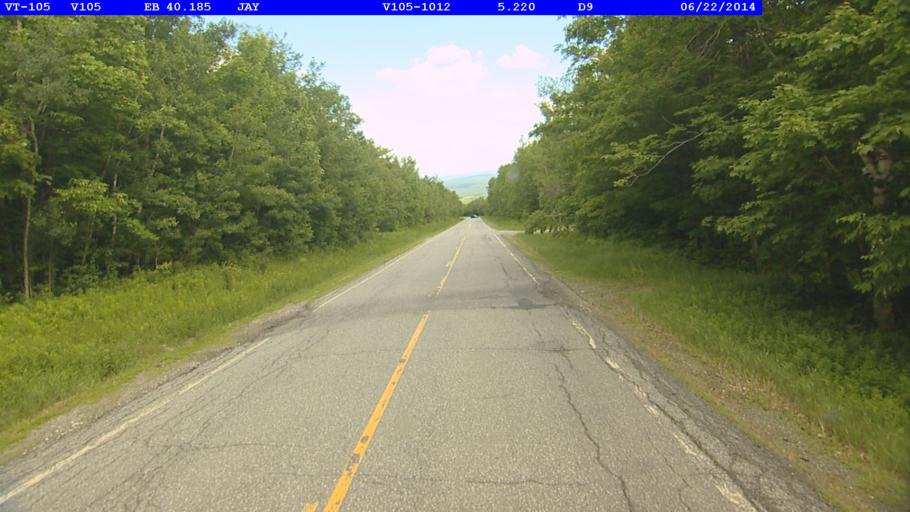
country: CA
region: Quebec
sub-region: Monteregie
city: Sutton
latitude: 44.9789
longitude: -72.4811
